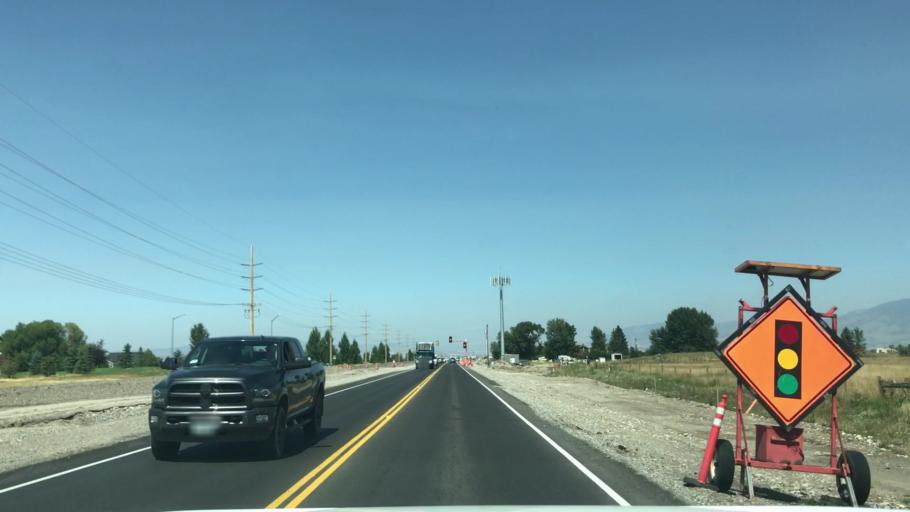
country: US
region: Montana
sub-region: Gallatin County
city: Belgrade
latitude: 45.7198
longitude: -111.1851
